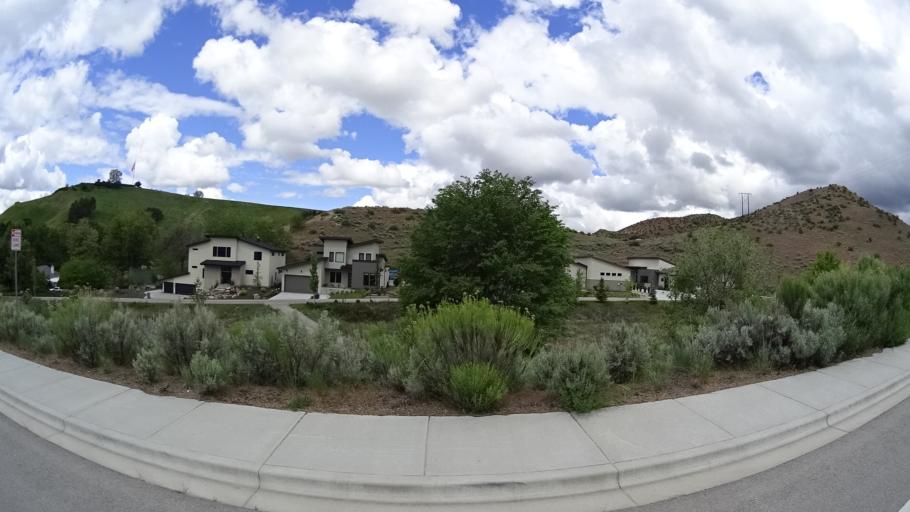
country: US
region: Idaho
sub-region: Ada County
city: Boise
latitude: 43.6530
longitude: -116.1919
